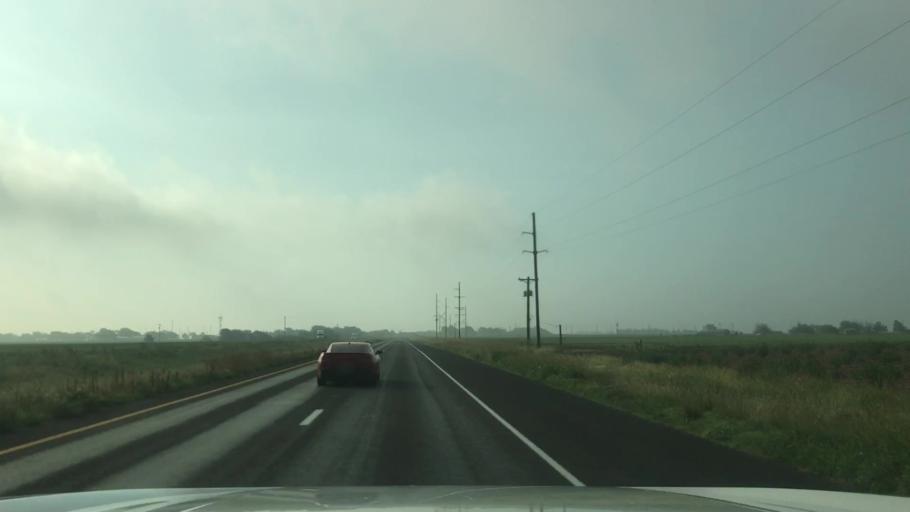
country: US
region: Texas
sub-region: Lubbock County
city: Slaton
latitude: 33.3651
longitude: -101.5640
